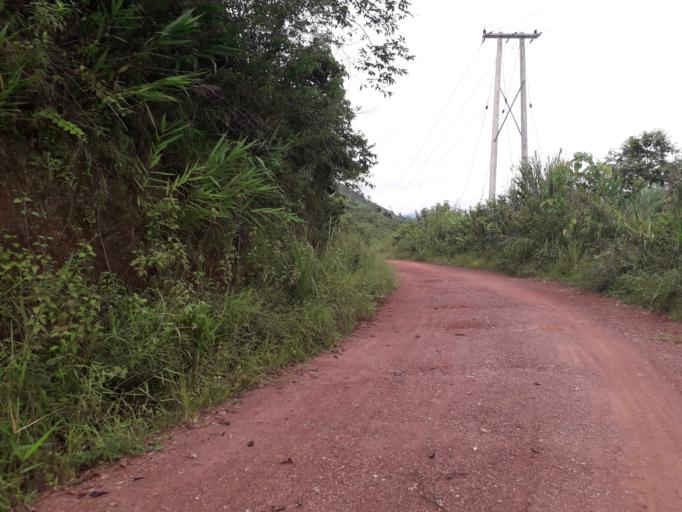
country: CN
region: Yunnan
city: Menglie
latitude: 22.2577
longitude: 101.5971
